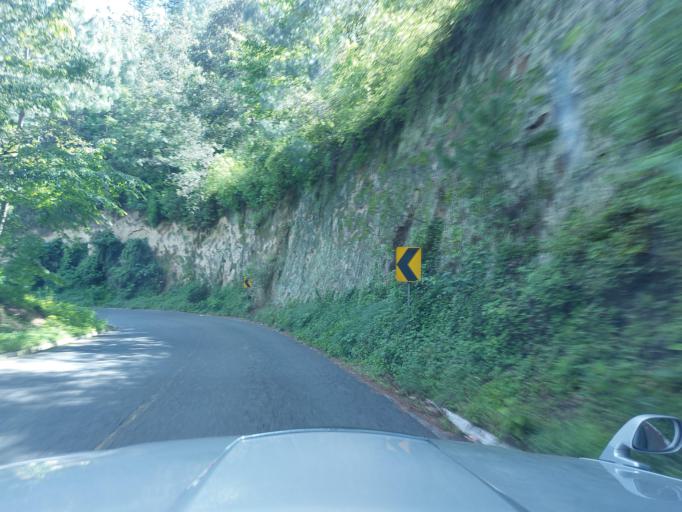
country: GT
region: Chimaltenango
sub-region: Municipio de Santa Cruz Balanya
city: Santa Cruz Balanya
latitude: 14.6917
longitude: -90.8973
